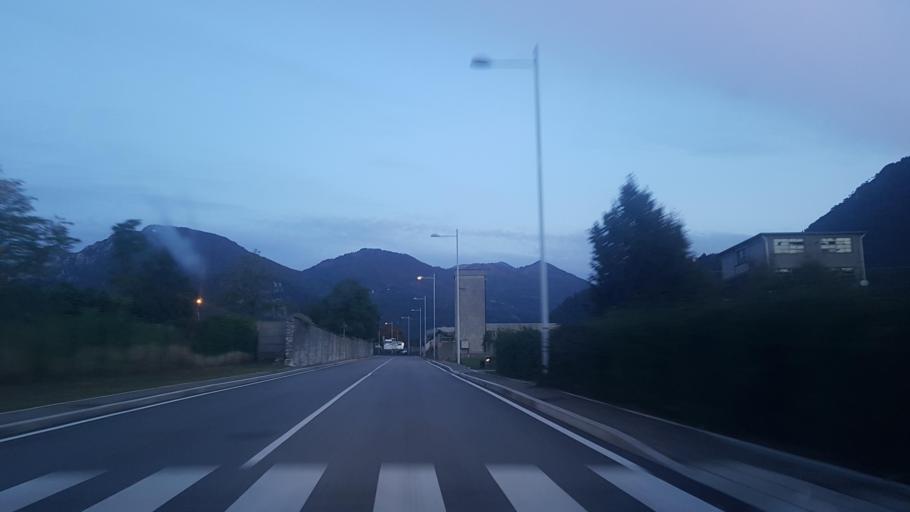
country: IT
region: Friuli Venezia Giulia
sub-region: Provincia di Udine
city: Tolmezzo
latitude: 46.3931
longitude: 13.0237
